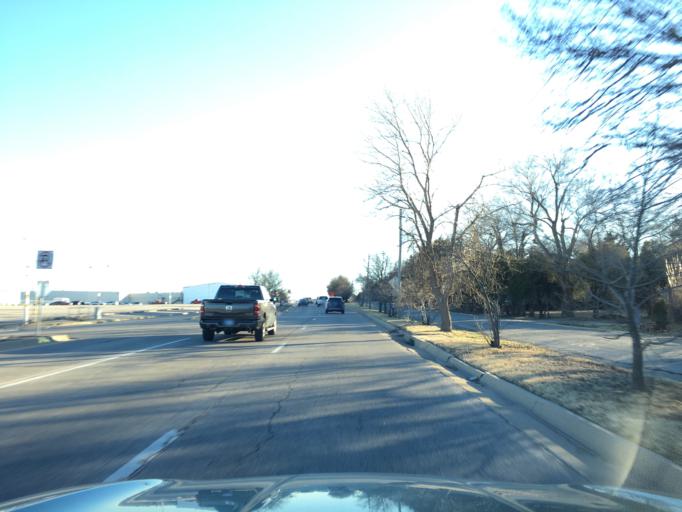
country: US
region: Kansas
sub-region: Sedgwick County
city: Bellaire
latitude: 37.6920
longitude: -97.2263
